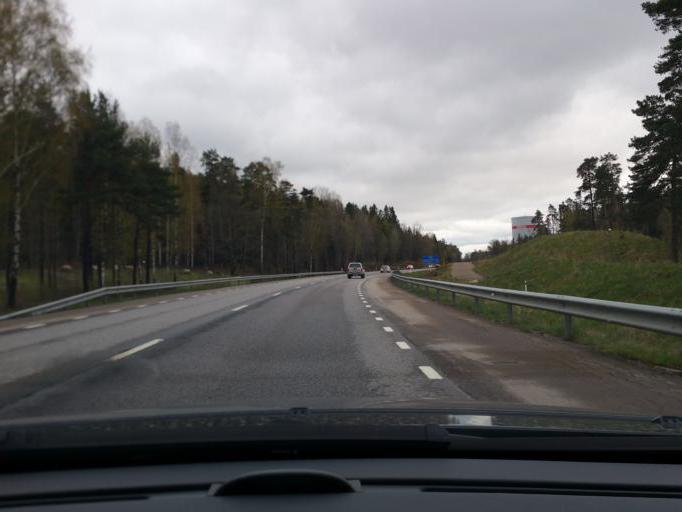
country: SE
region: Kronoberg
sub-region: Vaxjo Kommun
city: Vaexjoe
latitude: 56.8765
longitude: 14.8359
